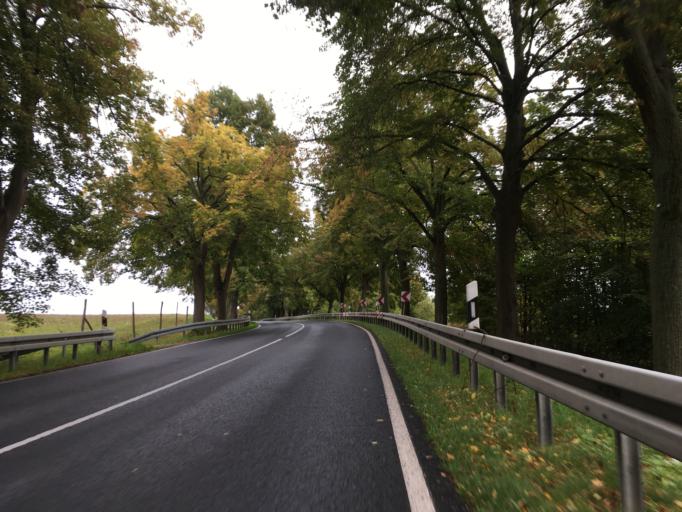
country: DE
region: Brandenburg
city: Werftpfuhl
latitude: 52.6844
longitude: 13.8455
